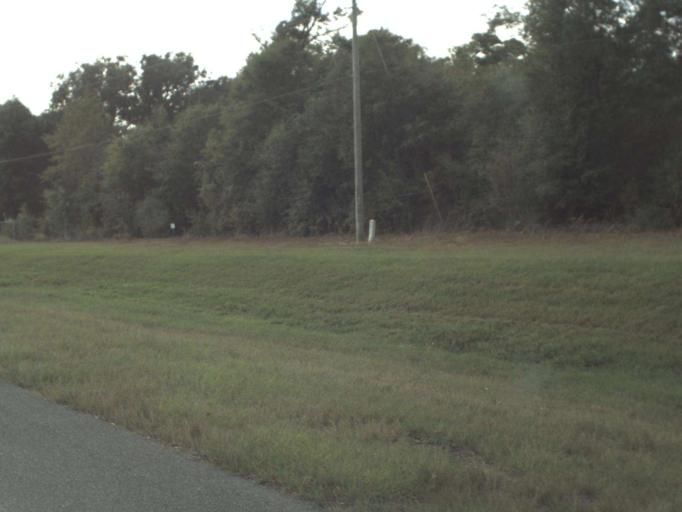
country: US
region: Florida
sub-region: Santa Rosa County
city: Point Baker
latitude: 30.7086
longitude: -87.0477
